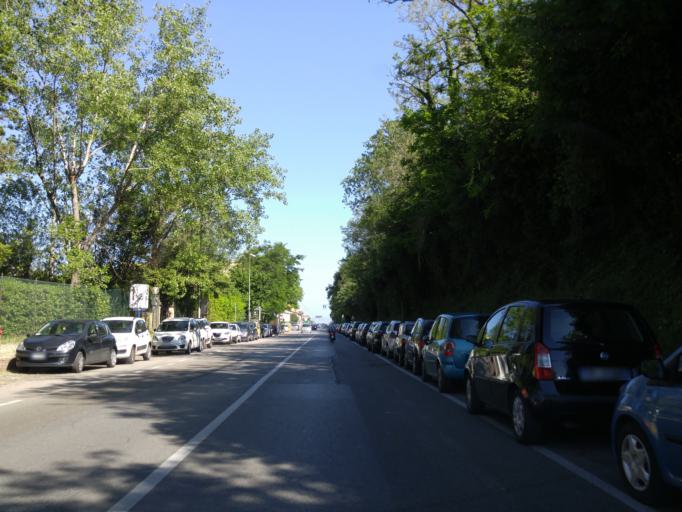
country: IT
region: The Marches
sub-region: Provincia di Pesaro e Urbino
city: Pesaro
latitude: 43.9028
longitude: 12.9316
